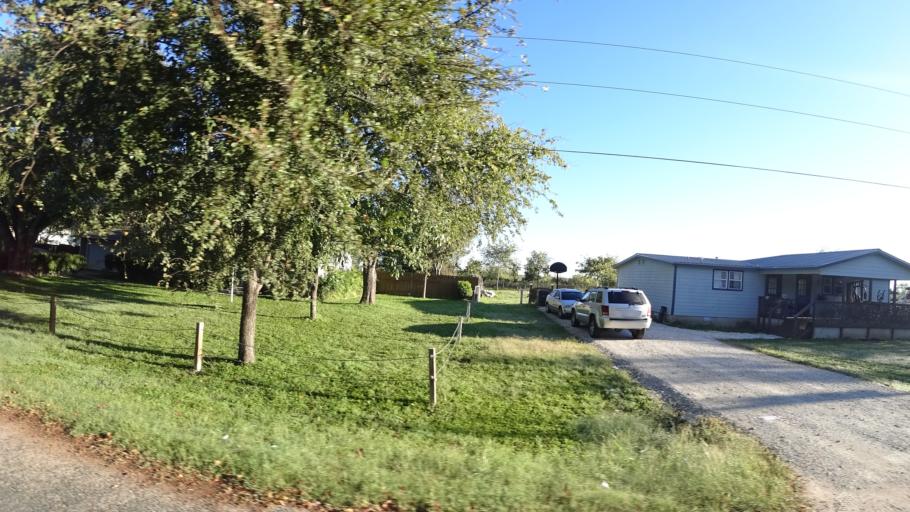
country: US
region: Texas
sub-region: Travis County
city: Hornsby Bend
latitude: 30.2255
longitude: -97.6282
